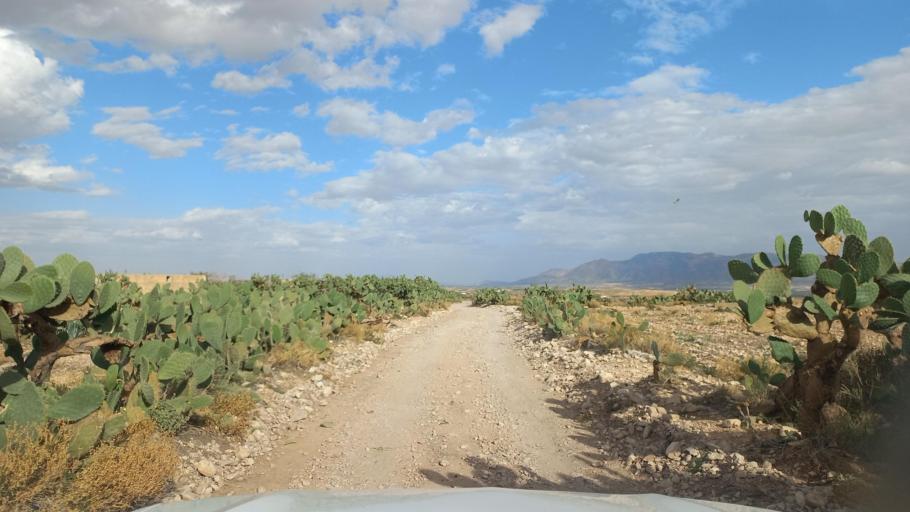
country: TN
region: Al Qasrayn
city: Sbiba
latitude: 35.4504
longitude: 9.0868
